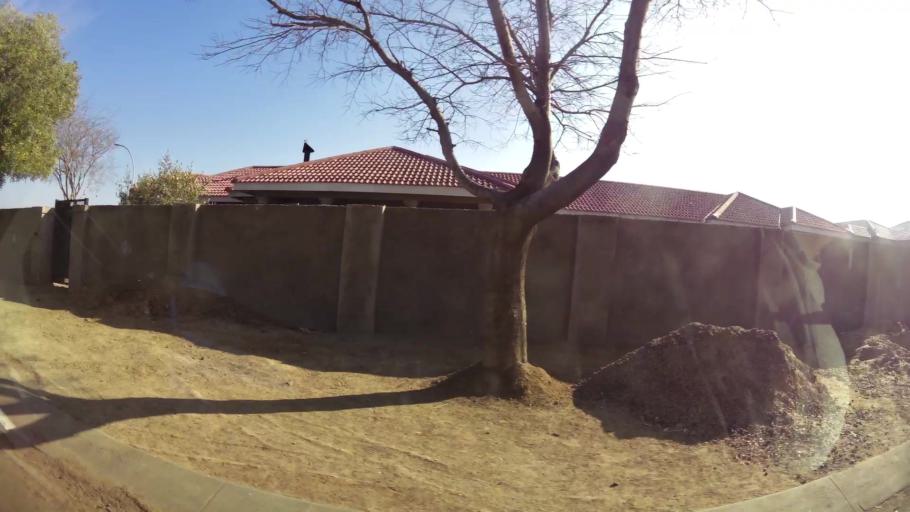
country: ZA
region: Orange Free State
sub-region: Mangaung Metropolitan Municipality
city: Bloemfontein
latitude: -29.1816
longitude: 26.1797
